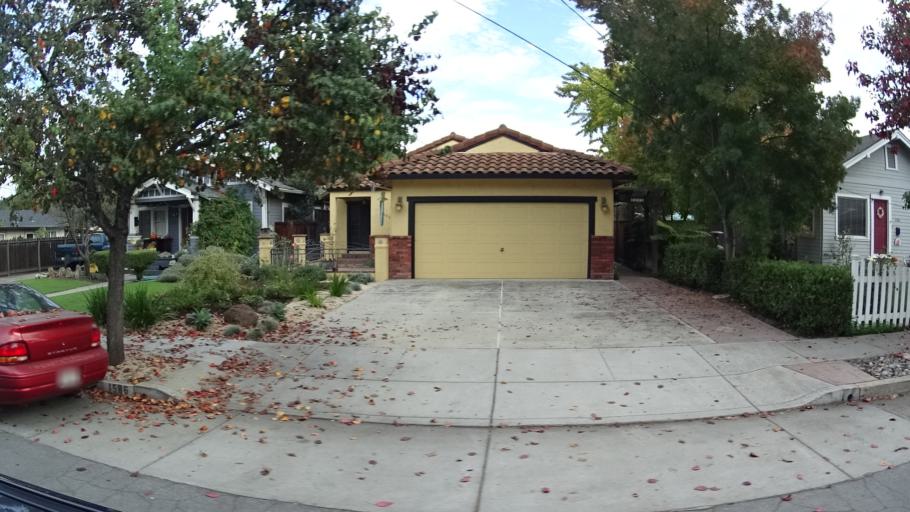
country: US
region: California
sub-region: Santa Clara County
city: Buena Vista
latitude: 37.3259
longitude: -121.9192
